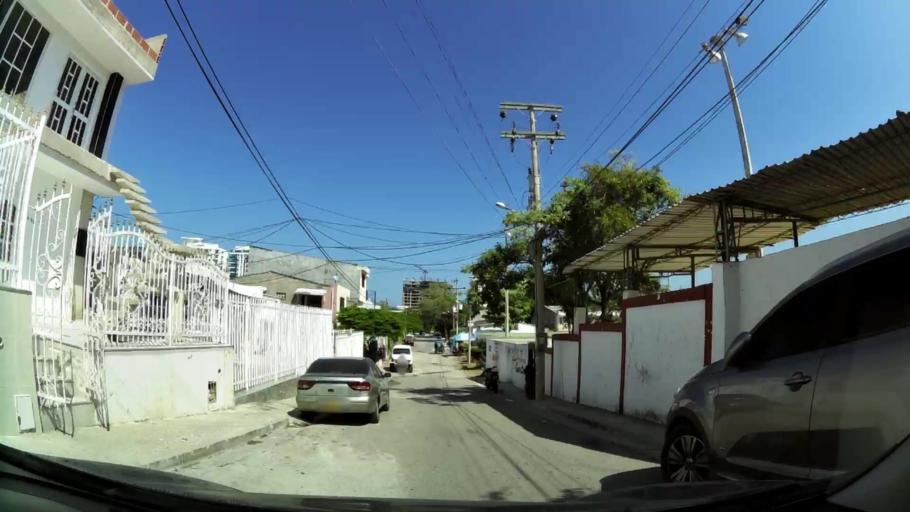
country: CO
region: Bolivar
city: Cartagena
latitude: 10.4407
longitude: -75.5202
